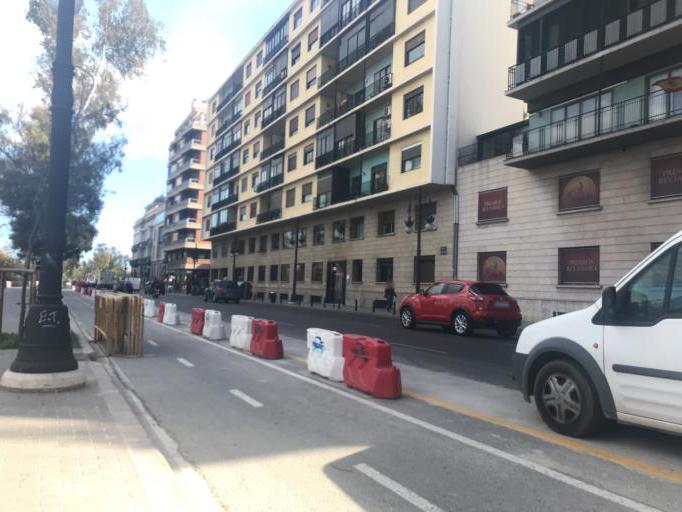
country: ES
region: Valencia
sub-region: Provincia de Valencia
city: Valencia
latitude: 39.4781
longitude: -0.3725
